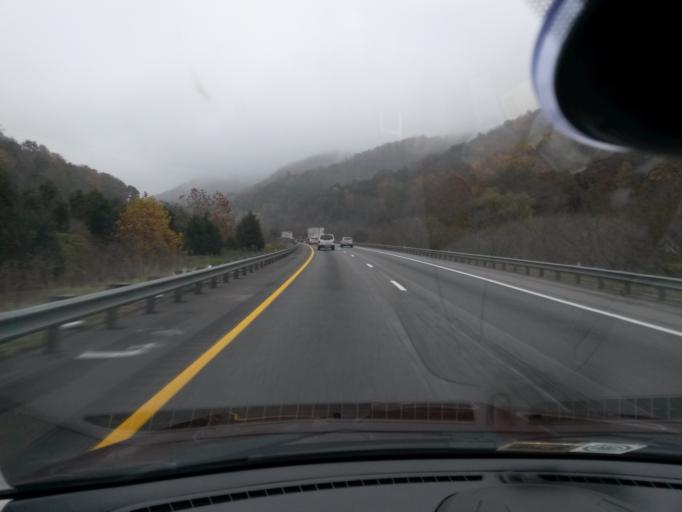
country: US
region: Virginia
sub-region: Montgomery County
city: Shawsville
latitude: 37.2265
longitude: -80.2487
